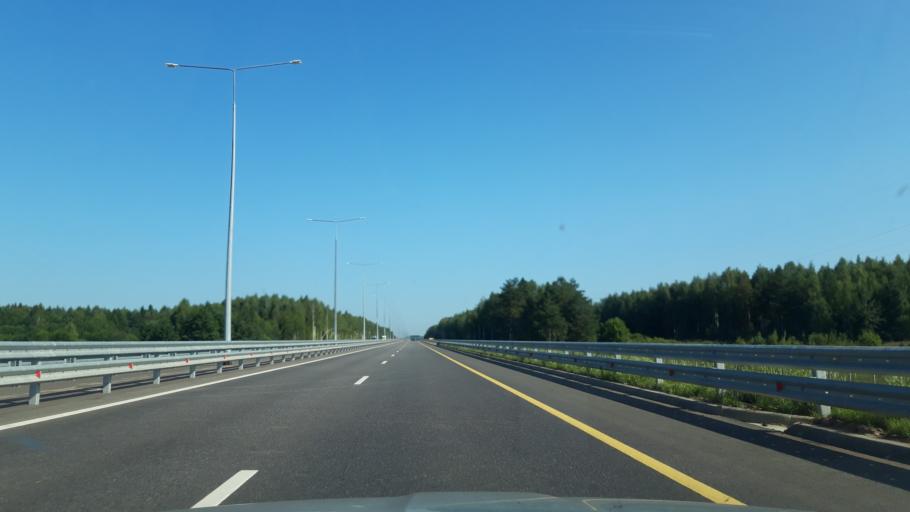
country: RU
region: Tverskaya
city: Zavidovo
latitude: 56.5299
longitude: 36.4982
